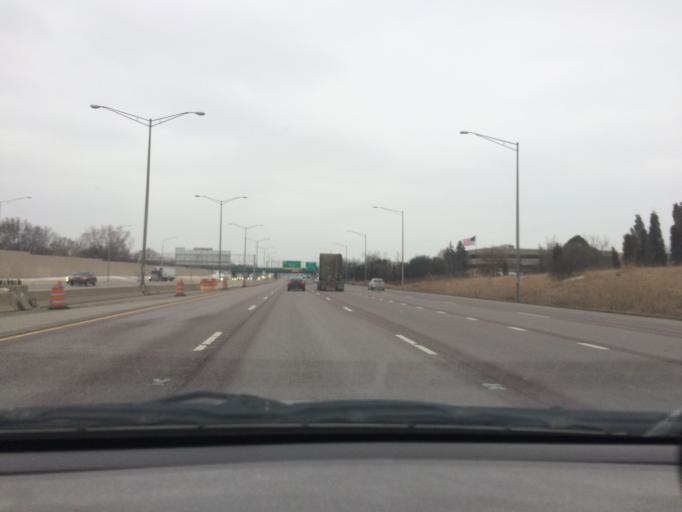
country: US
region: Illinois
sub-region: DuPage County
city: Itasca
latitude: 41.9776
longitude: -88.0240
